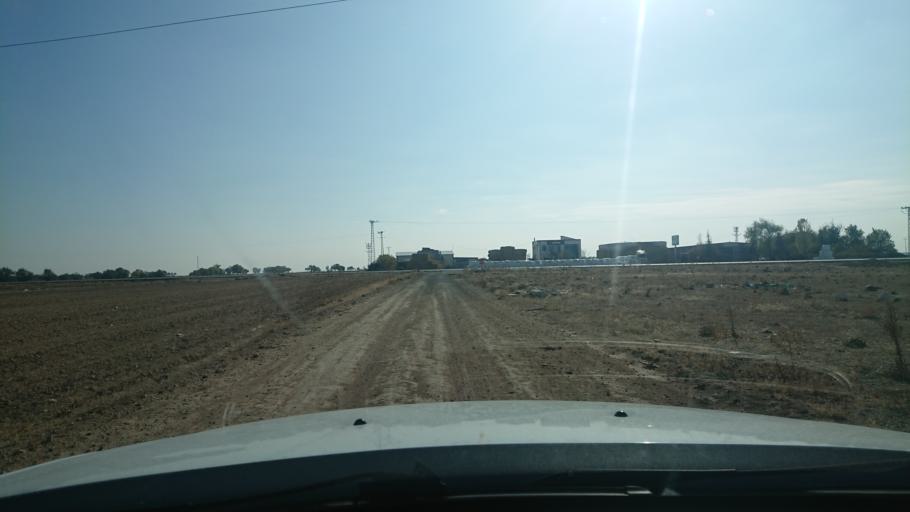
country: TR
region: Aksaray
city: Sultanhani
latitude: 38.2530
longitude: 33.4722
